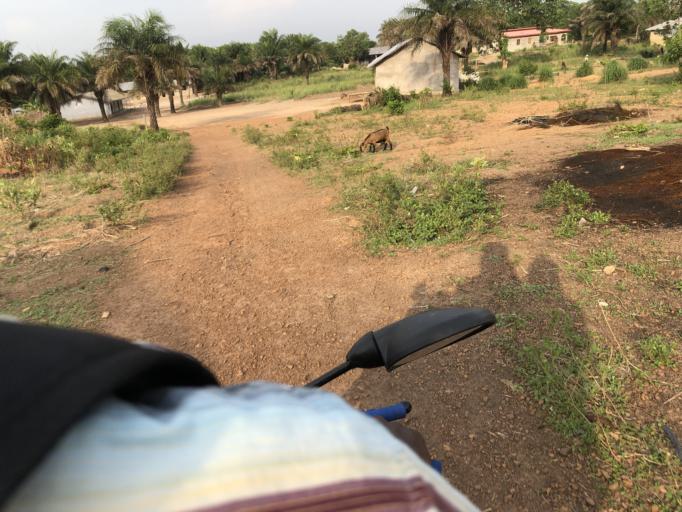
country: SL
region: Northern Province
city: Yonibana
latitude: 8.4630
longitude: -12.2044
